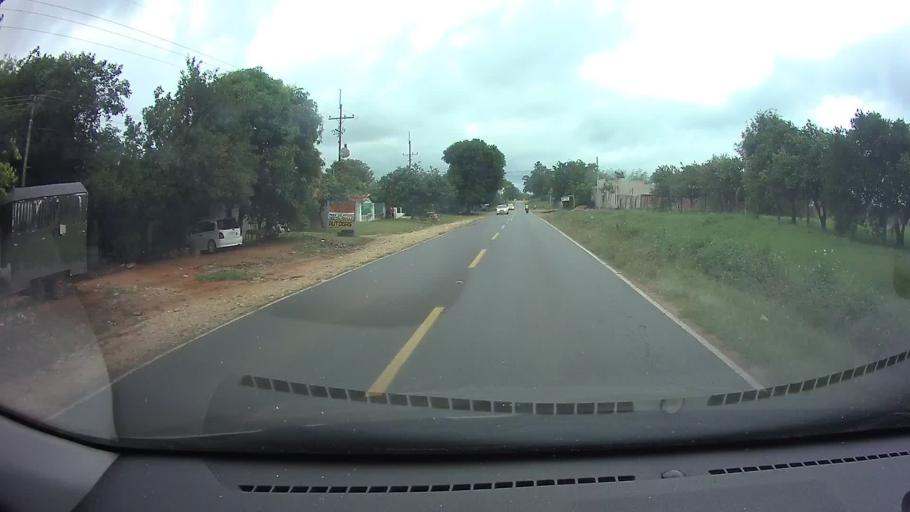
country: PY
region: Central
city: Guarambare
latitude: -25.5023
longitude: -57.4819
